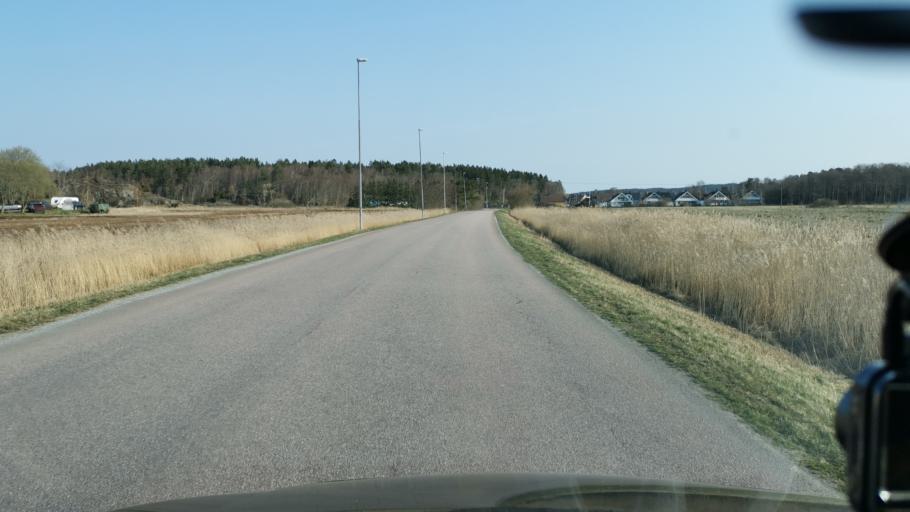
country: SE
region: Vaestra Goetaland
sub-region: Kungalvs Kommun
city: Kode
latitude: 57.9401
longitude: 11.8350
